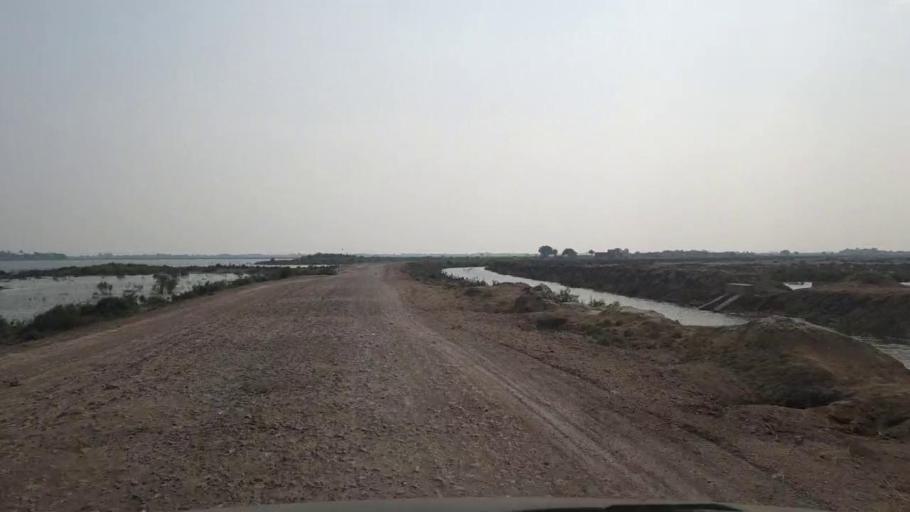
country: PK
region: Sindh
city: Tando Muhammad Khan
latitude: 25.0850
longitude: 68.3871
